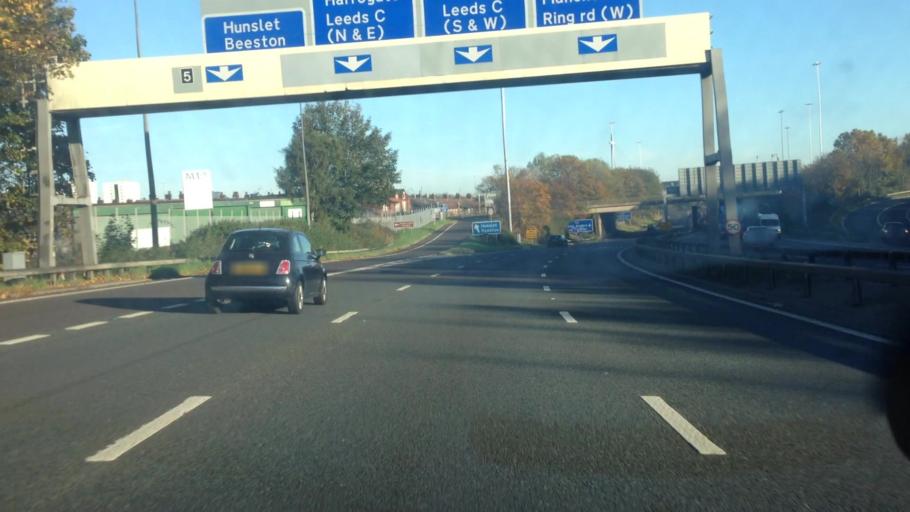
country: GB
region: England
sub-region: City and Borough of Leeds
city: Leeds
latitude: 53.7742
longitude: -1.5402
